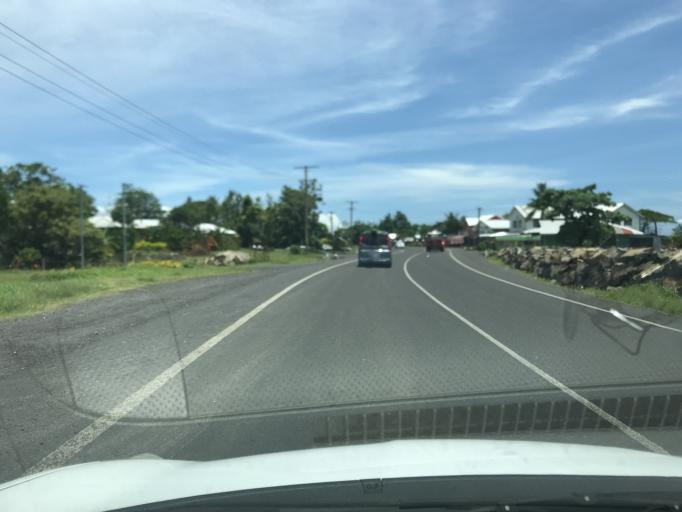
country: WS
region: Tuamasaga
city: Afenga
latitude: -13.8026
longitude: -171.8947
